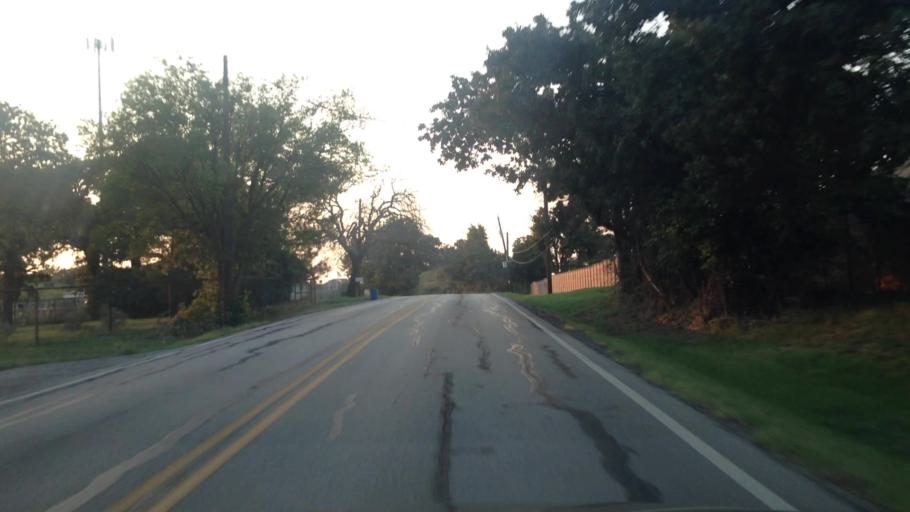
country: US
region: Texas
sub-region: Tarrant County
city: Kennedale
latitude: 32.6357
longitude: -97.2042
